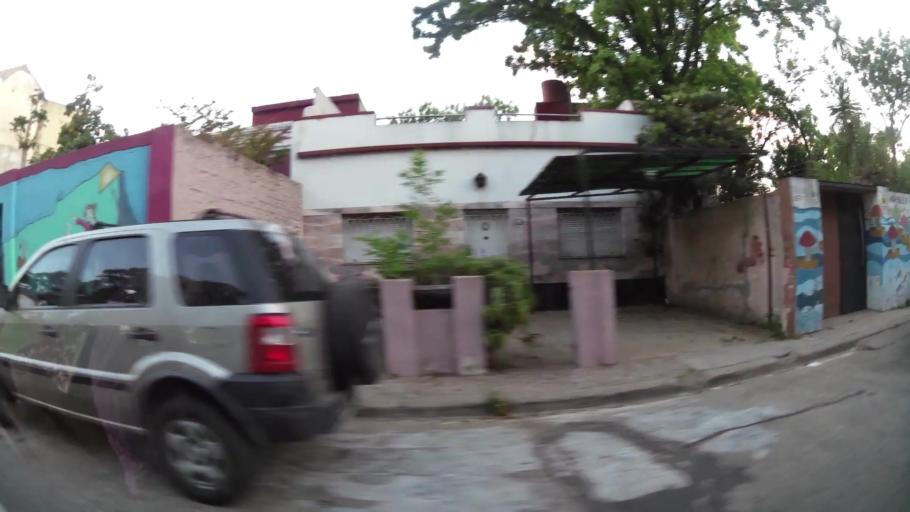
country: AR
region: Buenos Aires F.D.
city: Colegiales
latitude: -34.5516
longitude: -58.4783
